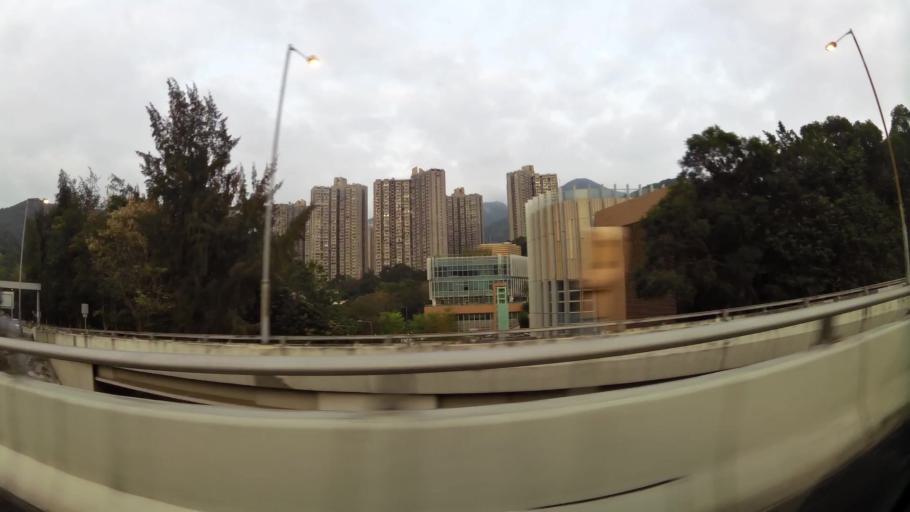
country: HK
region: Sha Tin
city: Sha Tin
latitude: 22.3803
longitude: 114.2103
